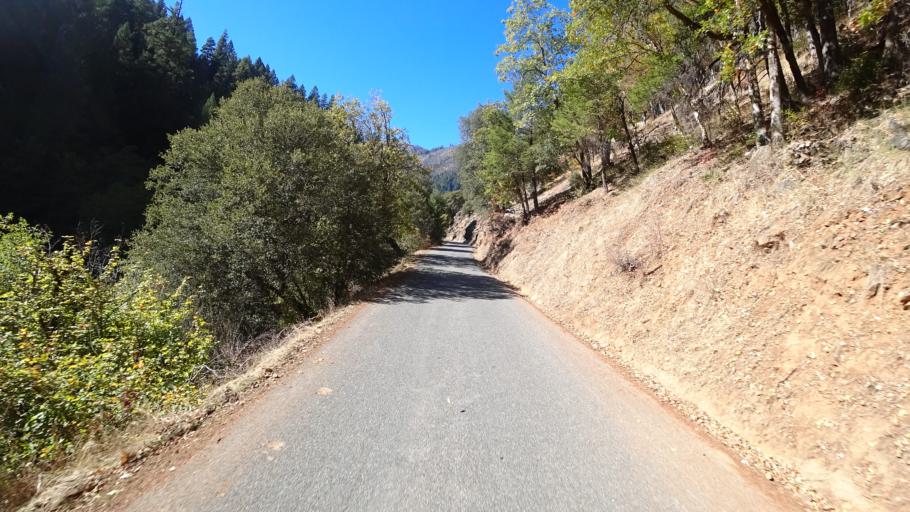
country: US
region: California
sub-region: Siskiyou County
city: Happy Camp
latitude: 41.3186
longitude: -123.1723
